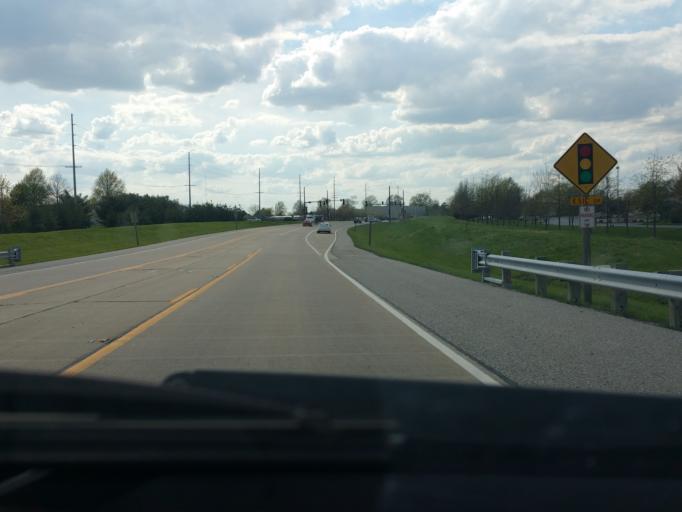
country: US
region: Illinois
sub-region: Madison County
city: Edwardsville
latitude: 38.7872
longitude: -89.9627
